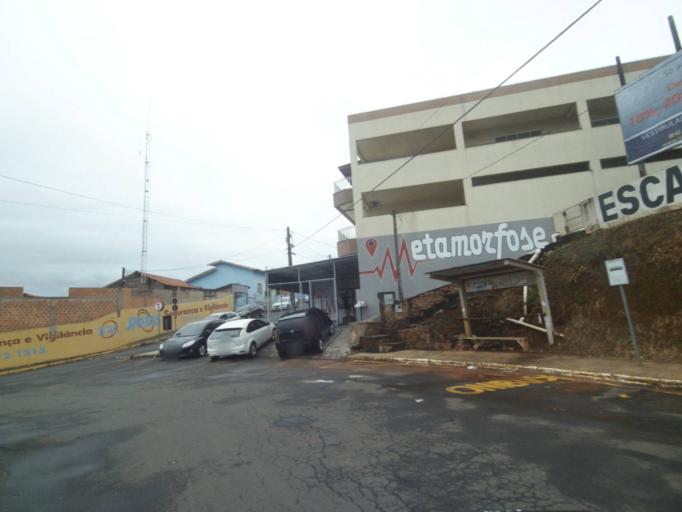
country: BR
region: Parana
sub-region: Telemaco Borba
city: Telemaco Borba
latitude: -24.3242
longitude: -50.6284
